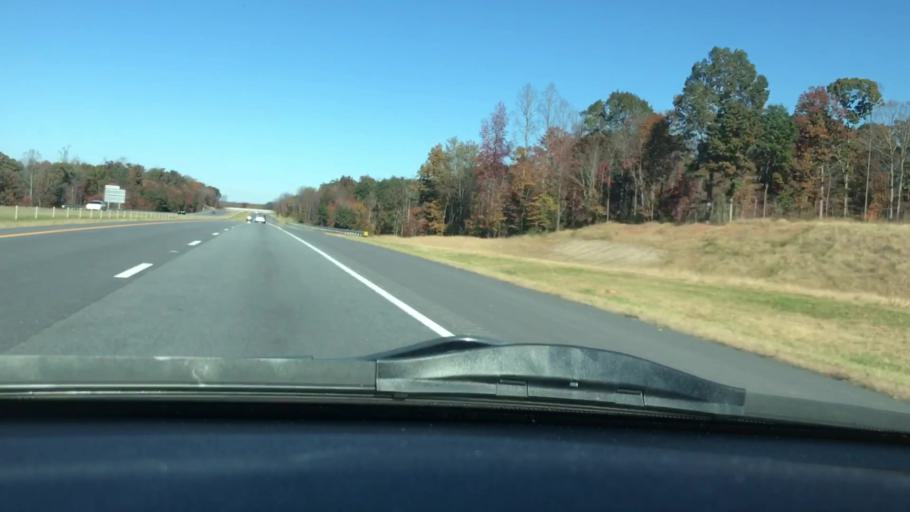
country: US
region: North Carolina
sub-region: Guilford County
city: Summerfield
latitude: 36.2051
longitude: -79.9257
